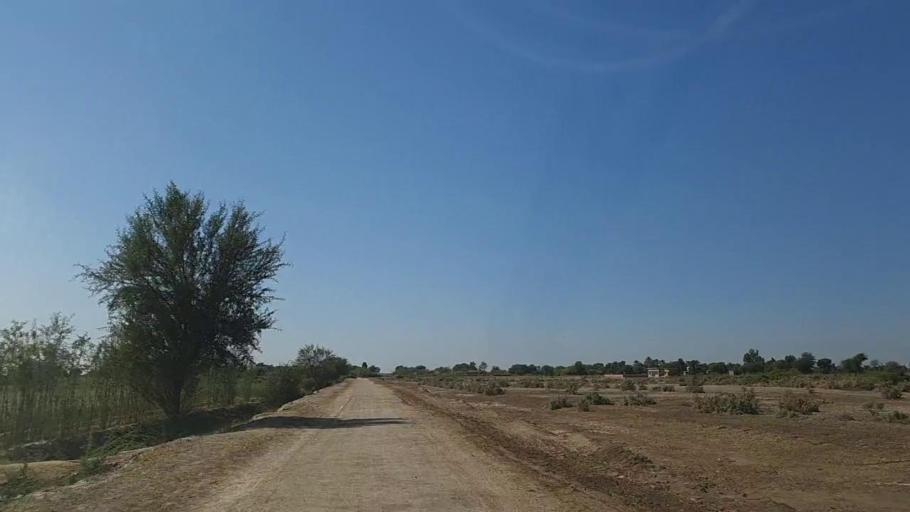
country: PK
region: Sindh
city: Kunri
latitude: 25.2823
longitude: 69.5169
